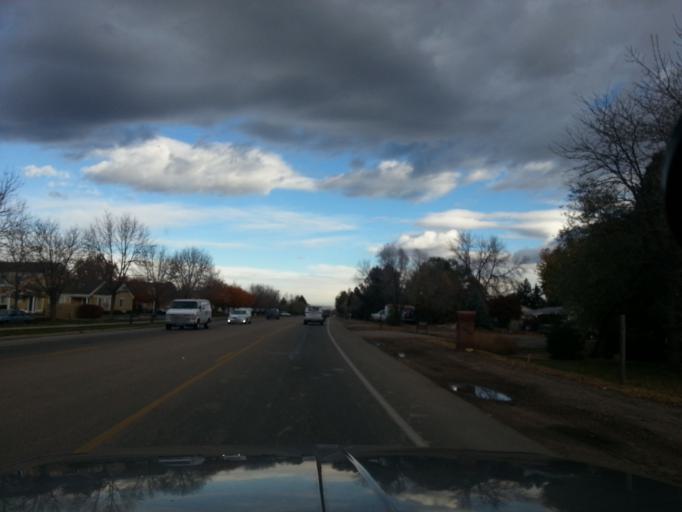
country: US
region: Colorado
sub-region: Larimer County
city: Fort Collins
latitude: 40.5326
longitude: -105.1153
